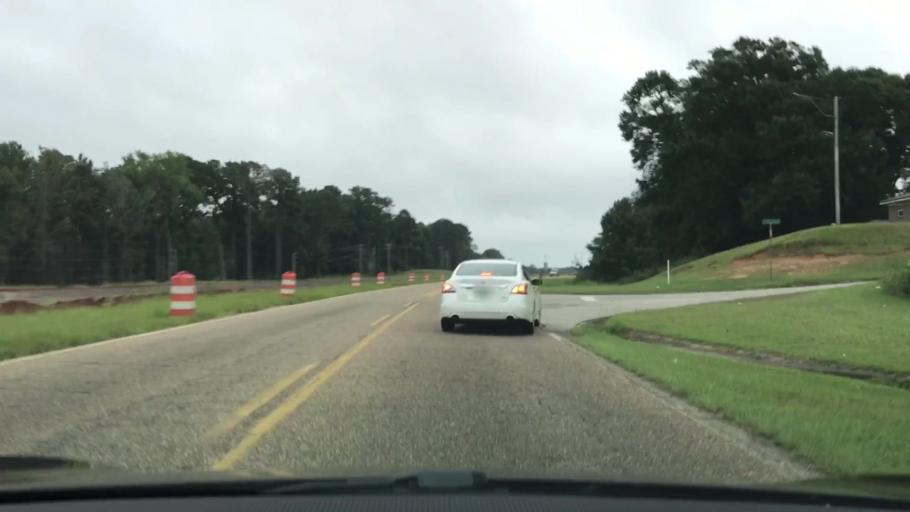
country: US
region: Alabama
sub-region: Coffee County
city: Elba
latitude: 31.4262
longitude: -86.0787
